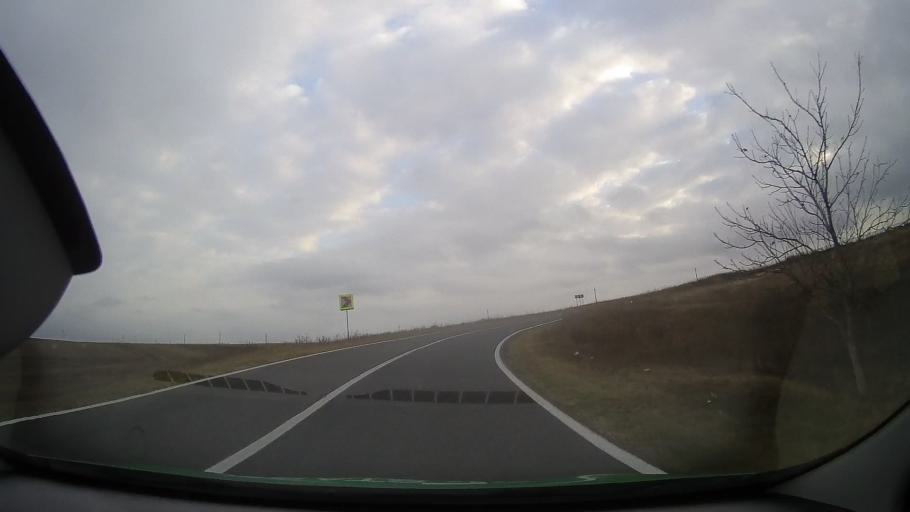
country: RO
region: Constanta
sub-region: Comuna Deleni
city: Deleni
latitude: 44.0939
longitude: 28.0173
